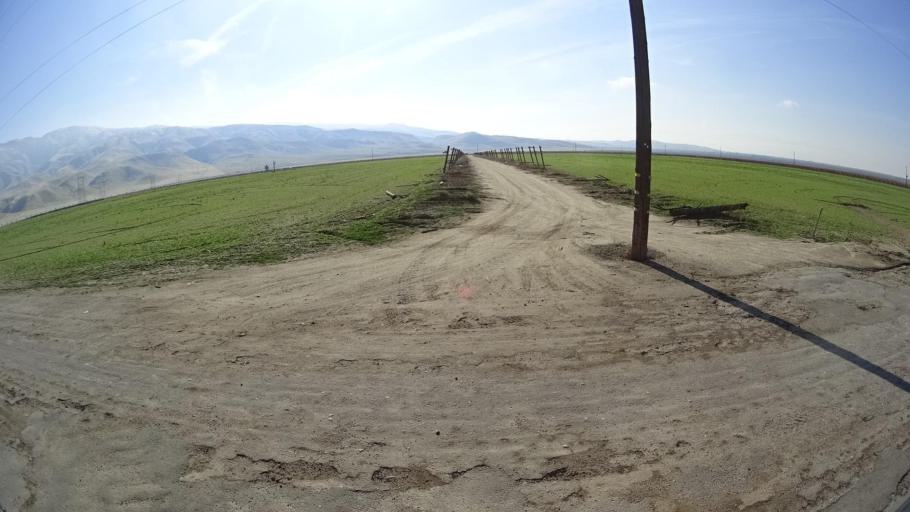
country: US
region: California
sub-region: Kern County
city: Arvin
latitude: 35.1961
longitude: -118.7883
